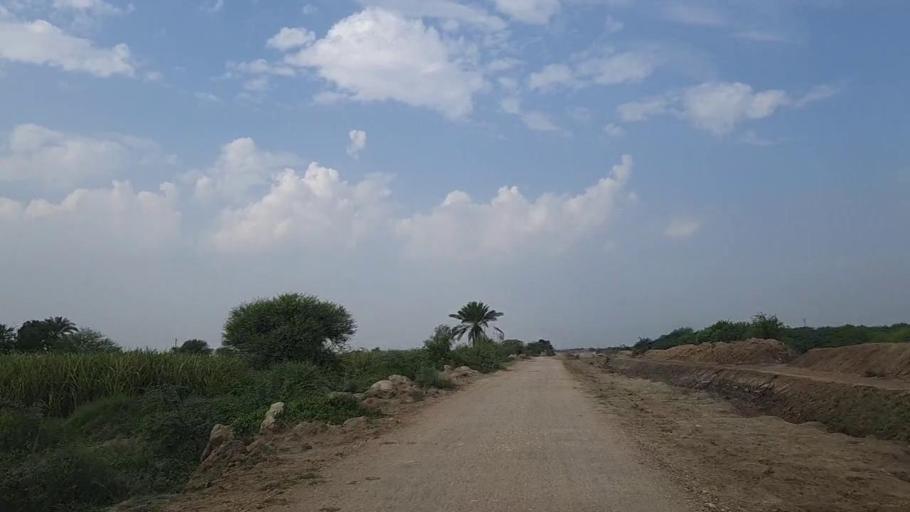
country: PK
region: Sindh
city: Daro Mehar
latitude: 24.7190
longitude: 68.1390
